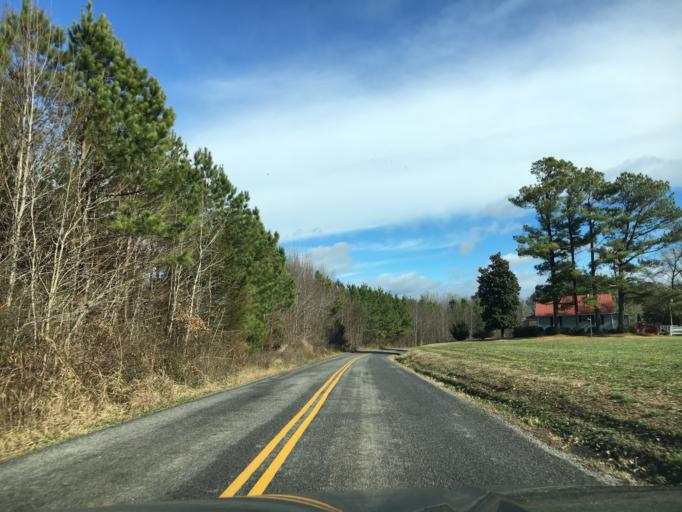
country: US
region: Virginia
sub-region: Amelia County
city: Amelia Court House
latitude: 37.4436
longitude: -78.0126
